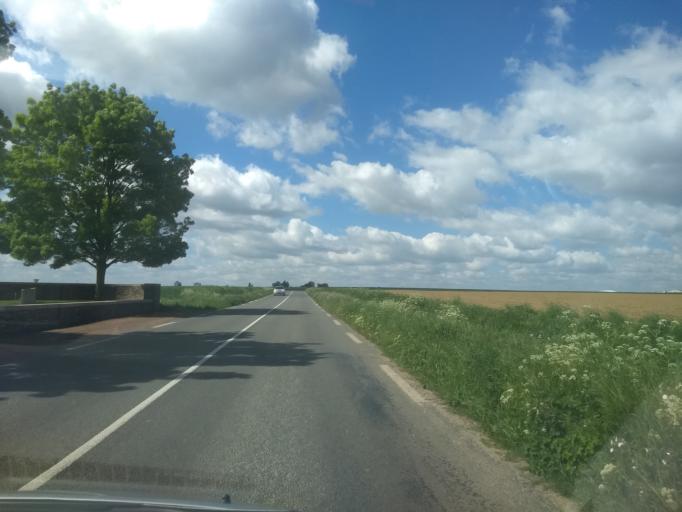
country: FR
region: Nord-Pas-de-Calais
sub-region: Departement du Pas-de-Calais
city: Saint-Laurent-Blangy
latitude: 50.3205
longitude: 2.8161
